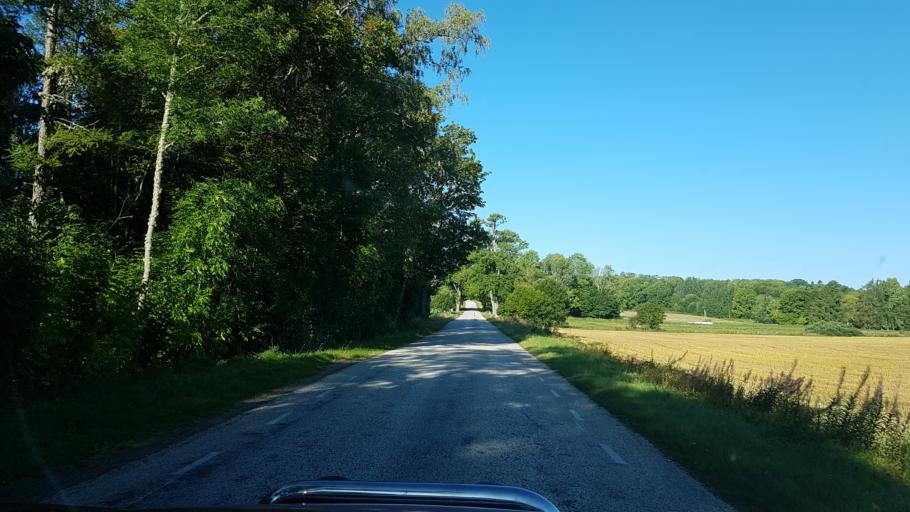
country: EE
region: Jogevamaa
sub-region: Tabivere vald
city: Tabivere
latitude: 58.6688
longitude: 26.7731
